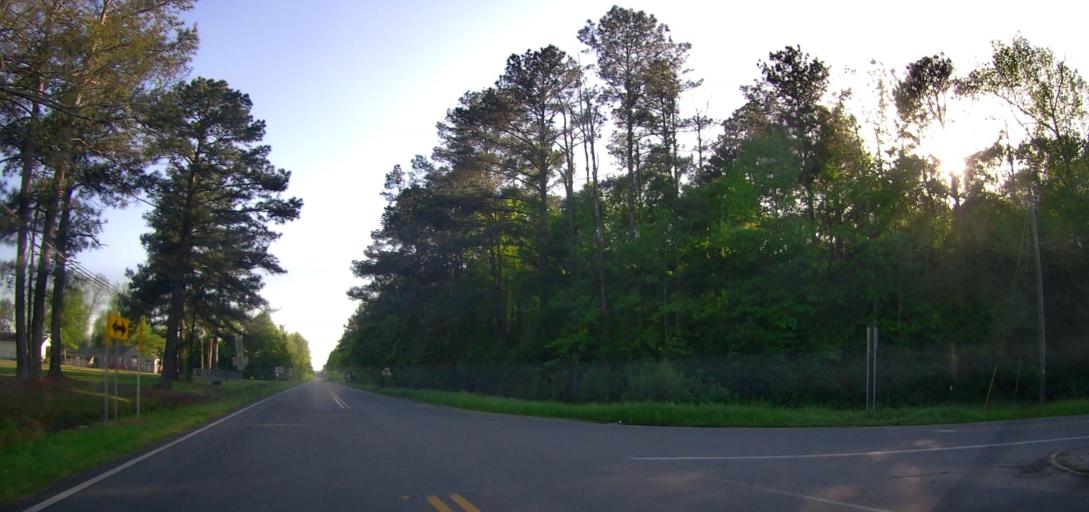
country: US
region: Georgia
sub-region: Macon County
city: Oglethorpe
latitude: 32.2834
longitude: -84.0714
